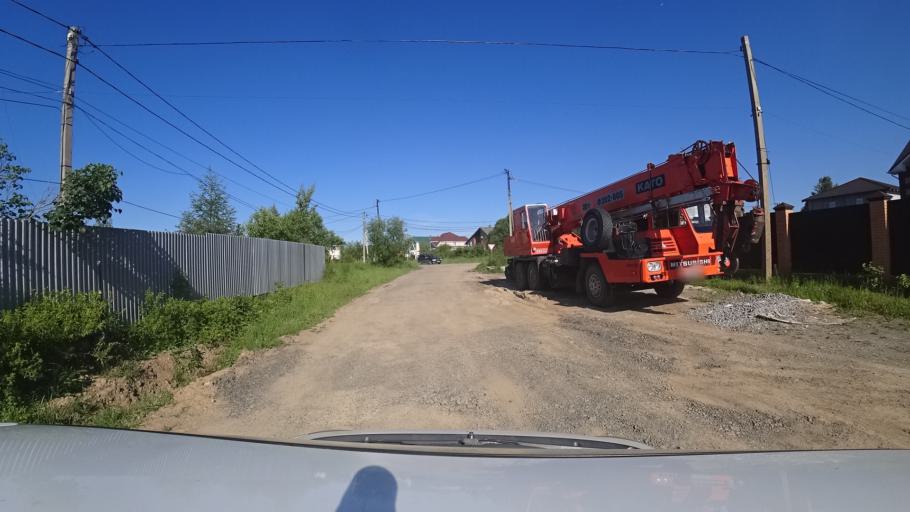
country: RU
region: Khabarovsk Krai
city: Topolevo
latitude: 48.5449
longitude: 135.1733
